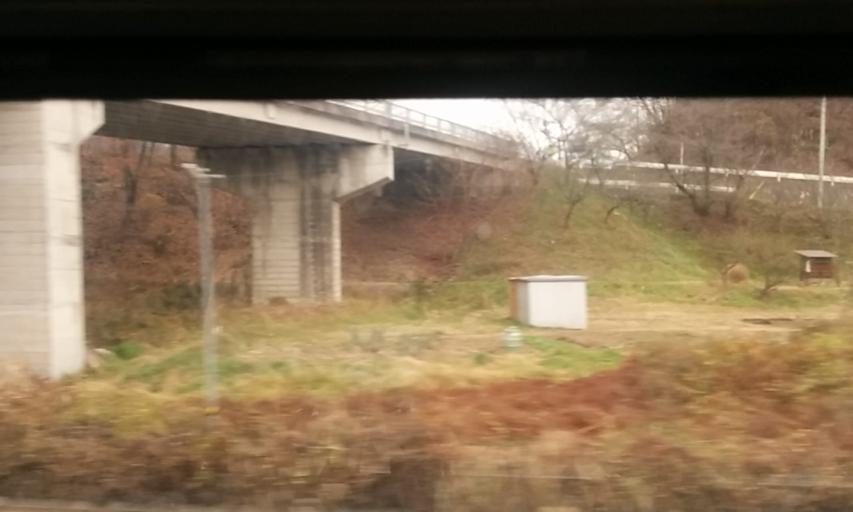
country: JP
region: Nagano
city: Hotaka
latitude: 36.3570
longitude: 137.9333
